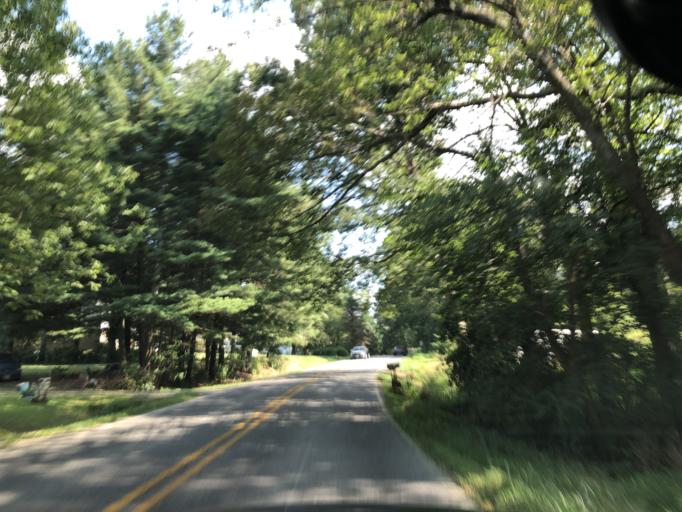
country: US
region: Maryland
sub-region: Frederick County
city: Linganore
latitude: 39.4042
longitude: -77.1985
